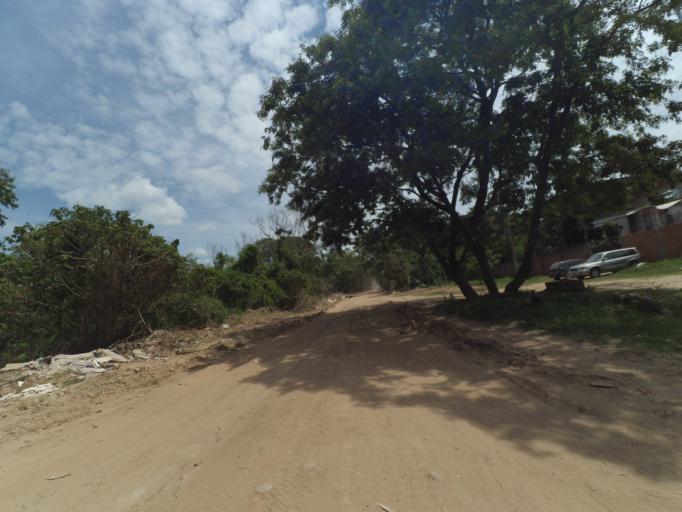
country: BO
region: Santa Cruz
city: Santa Cruz de la Sierra
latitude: -17.7884
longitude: -63.2243
